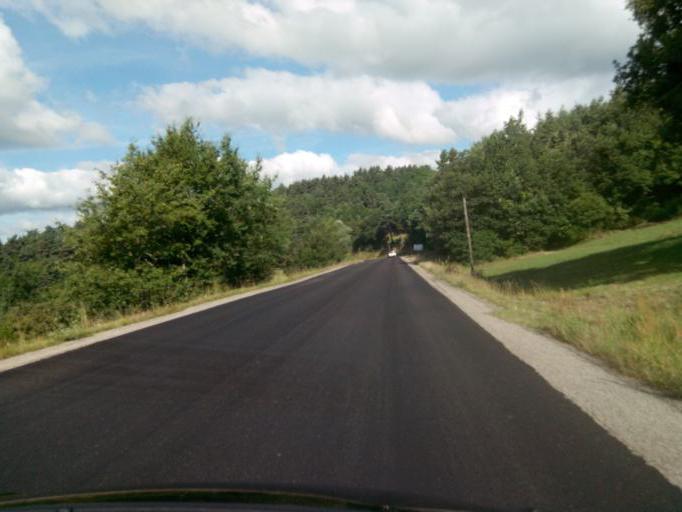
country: FR
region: Auvergne
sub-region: Departement de la Haute-Loire
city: Retournac
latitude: 45.2264
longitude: 4.0464
